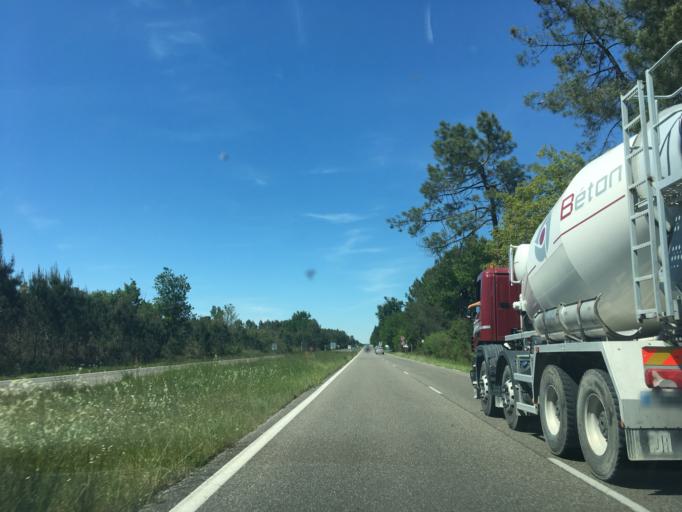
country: FR
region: Aquitaine
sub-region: Departement de la Gironde
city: Listrac-Medoc
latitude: 45.1023
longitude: -0.8029
